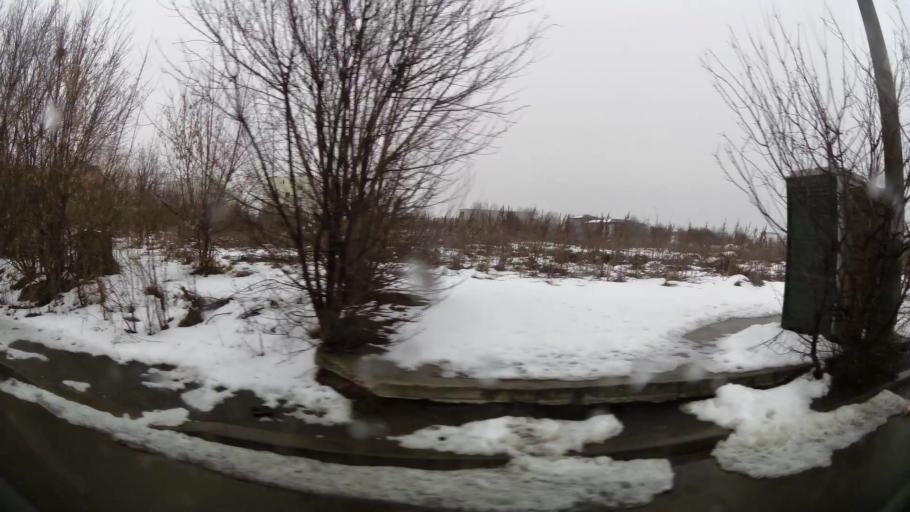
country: RO
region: Ilfov
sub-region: Comuna Otopeni
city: Otopeni
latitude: 44.4996
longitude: 26.0578
